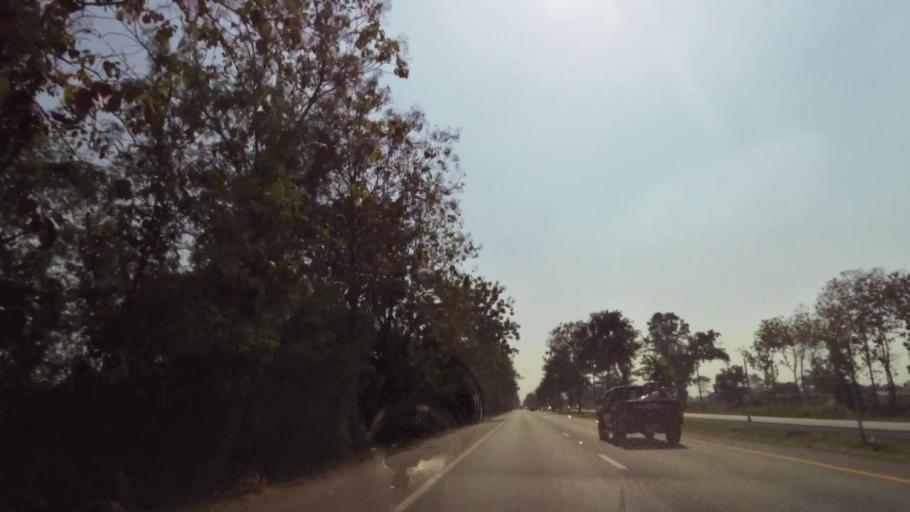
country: TH
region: Phichit
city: Bueng Na Rang
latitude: 16.0886
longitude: 100.1250
